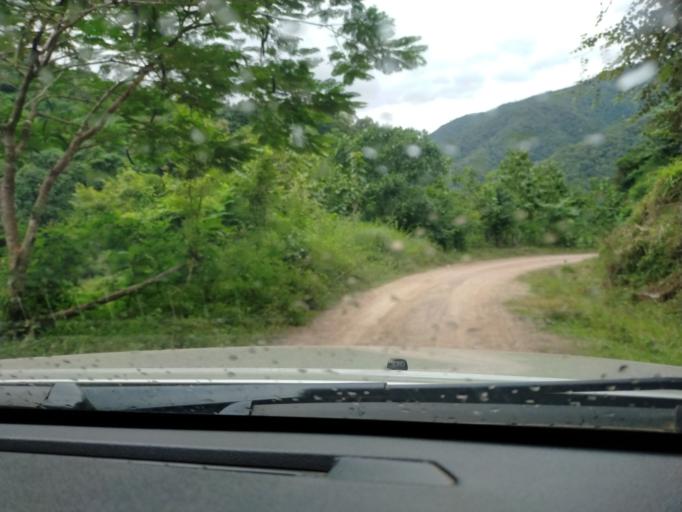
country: TH
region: Nan
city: Chaloem Phra Kiat
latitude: 19.8153
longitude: 101.3591
